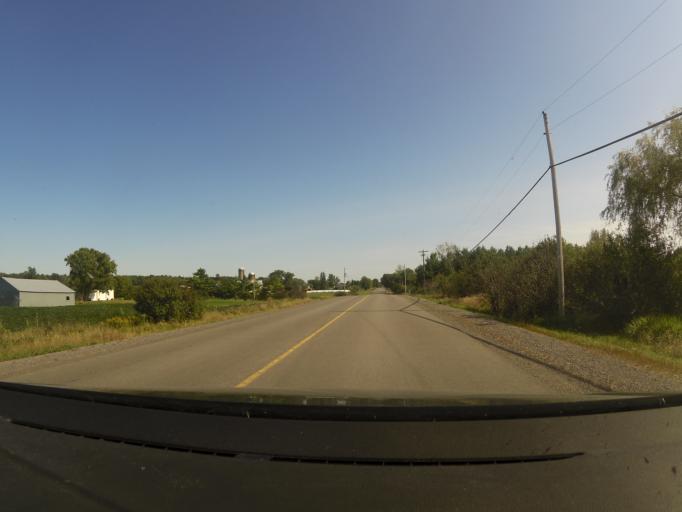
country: CA
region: Ontario
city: Arnprior
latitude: 45.4035
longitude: -76.1568
